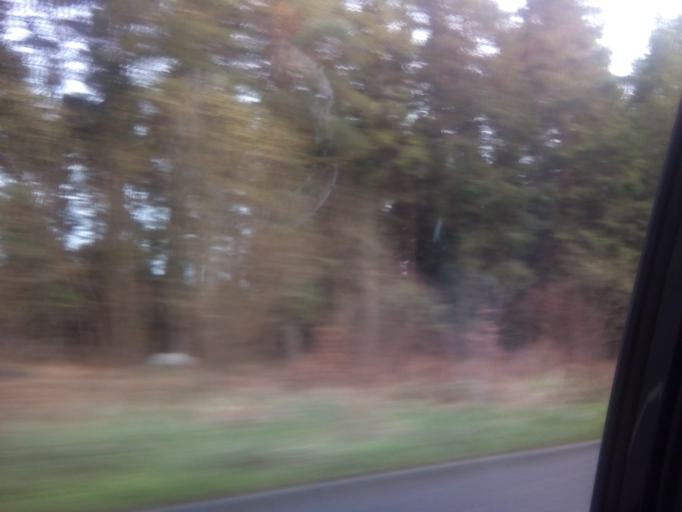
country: IE
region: Leinster
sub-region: Laois
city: Abbeyleix
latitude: 52.8942
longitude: -7.3615
